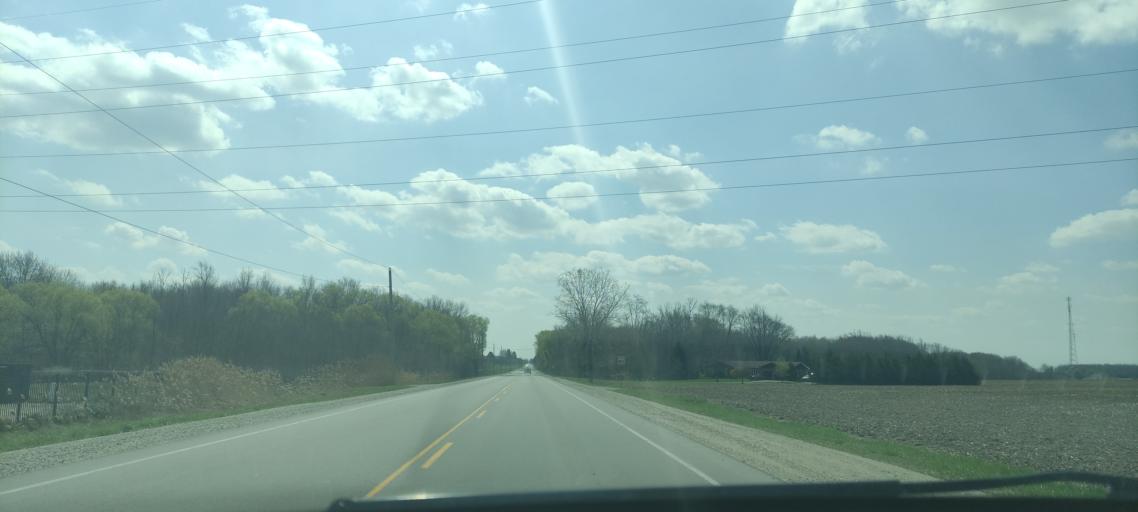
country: CA
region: Ontario
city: Stratford
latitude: 43.3448
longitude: -81.0007
